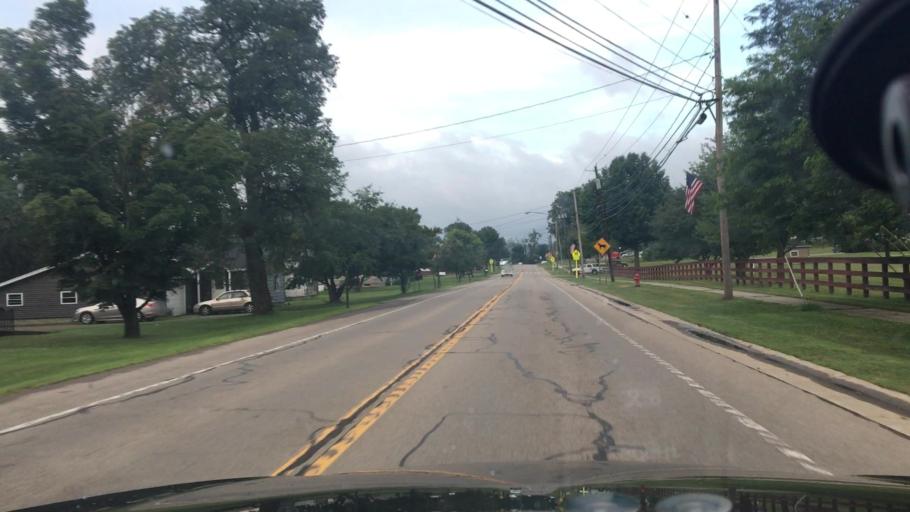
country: US
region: New York
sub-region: Cattaraugus County
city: Randolph
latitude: 42.1670
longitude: -78.9615
